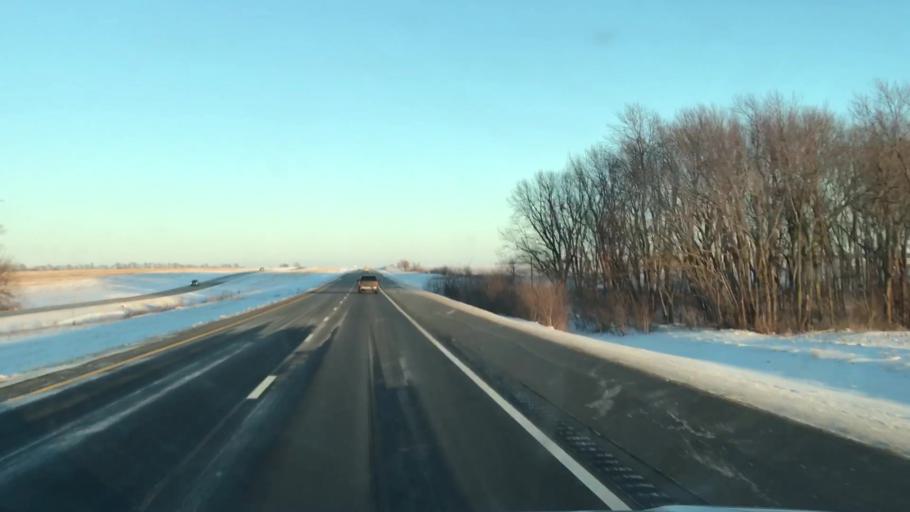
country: US
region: Missouri
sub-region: DeKalb County
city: Maysville
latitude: 39.7615
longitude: -94.3855
